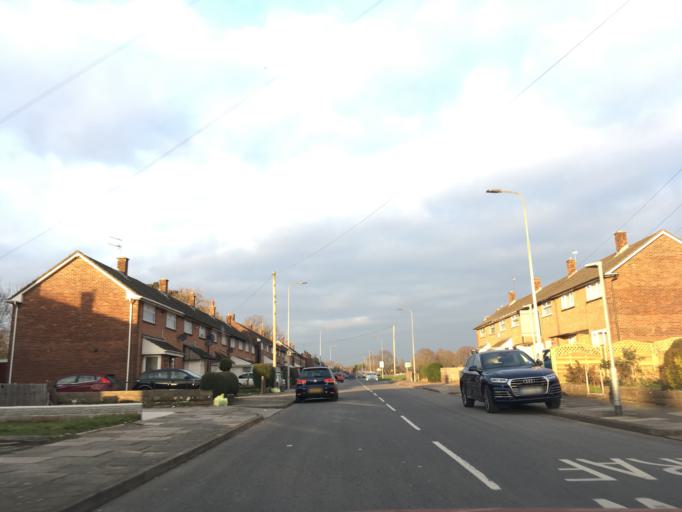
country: GB
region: Wales
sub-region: Newport
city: Marshfield
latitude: 51.5196
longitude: -3.1326
